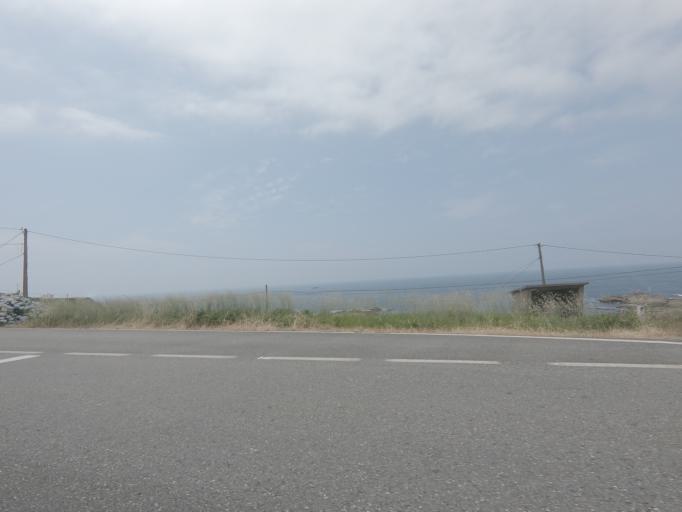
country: ES
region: Galicia
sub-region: Provincia de Pontevedra
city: O Rosal
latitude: 41.9519
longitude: -8.8825
